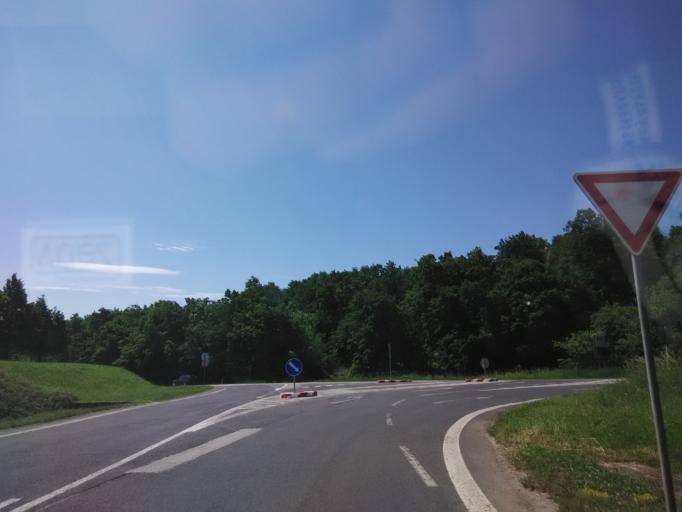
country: SK
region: Nitriansky
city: Tlmace
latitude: 48.2520
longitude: 18.4544
